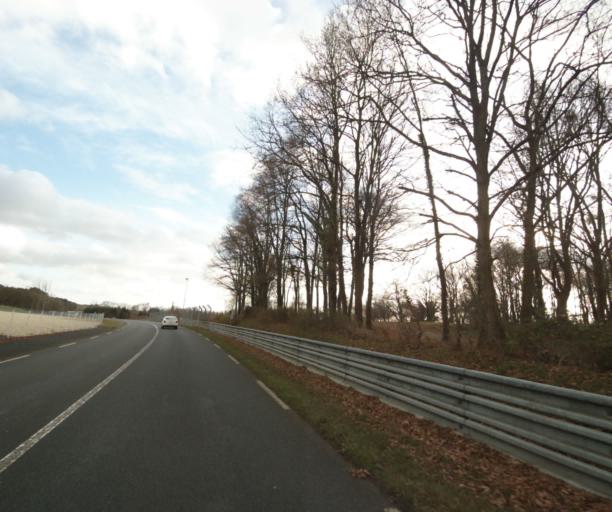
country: FR
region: Pays de la Loire
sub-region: Departement de la Sarthe
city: Arnage
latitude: 47.9338
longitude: 0.2082
